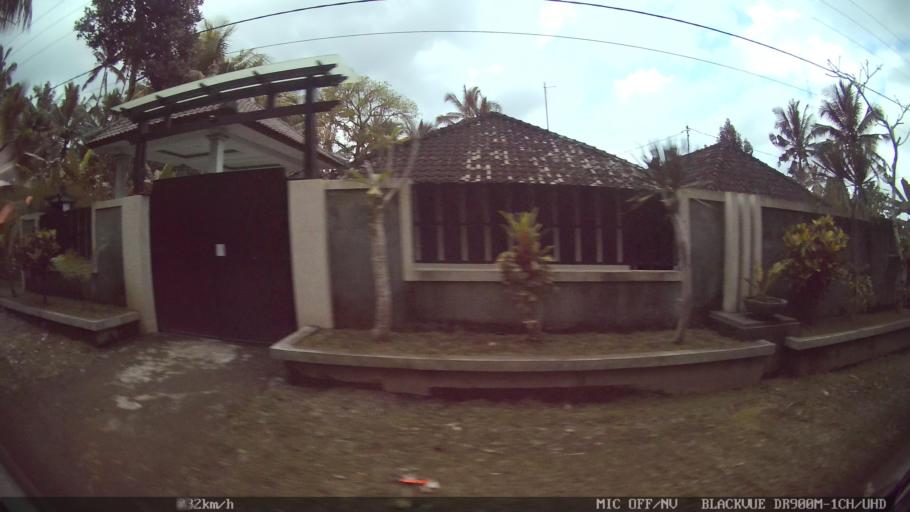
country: ID
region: Bali
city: Banjar Wangsian
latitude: -8.4517
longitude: 115.4200
